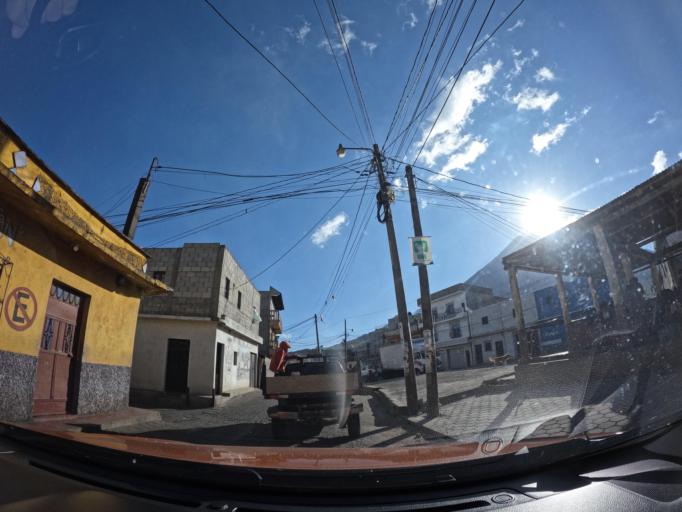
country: GT
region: Sacatepequez
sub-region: Municipio de Santa Maria de Jesus
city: Santa Maria de Jesus
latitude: 14.4919
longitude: -90.7086
